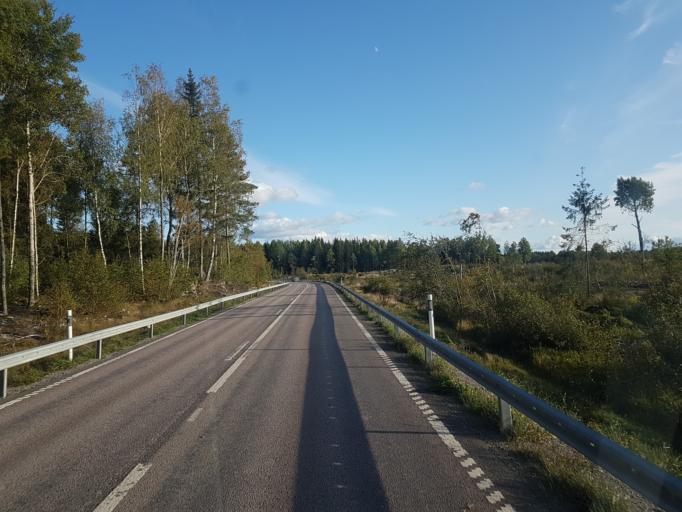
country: SE
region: Uppsala
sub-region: Heby Kommun
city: Heby
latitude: 59.8067
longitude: 16.7915
